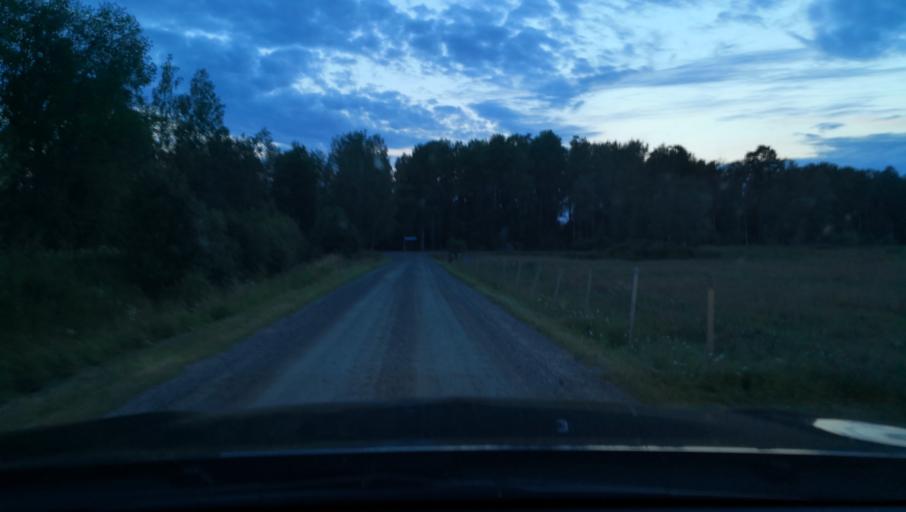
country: SE
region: Uppsala
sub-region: Heby Kommun
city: OEstervala
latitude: 60.0150
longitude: 17.2941
